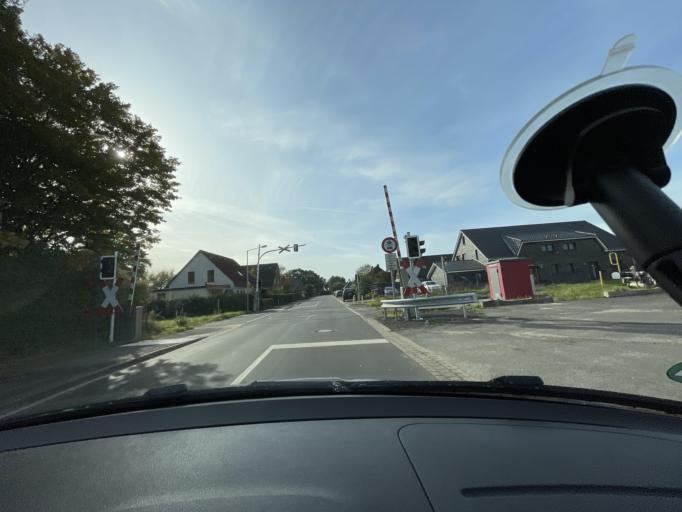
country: DE
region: Lower Saxony
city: Celle
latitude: 52.6379
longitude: 10.1110
